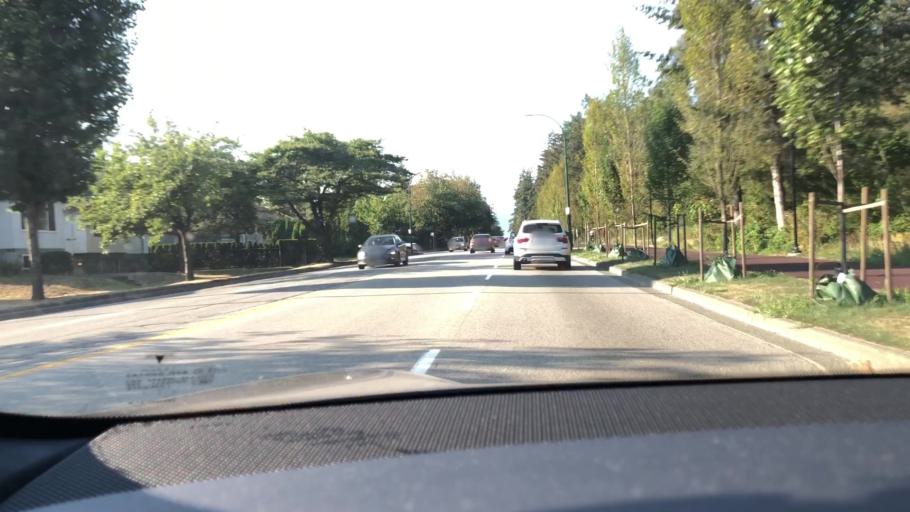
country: CA
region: British Columbia
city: Burnaby
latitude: 49.2255
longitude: -123.0235
